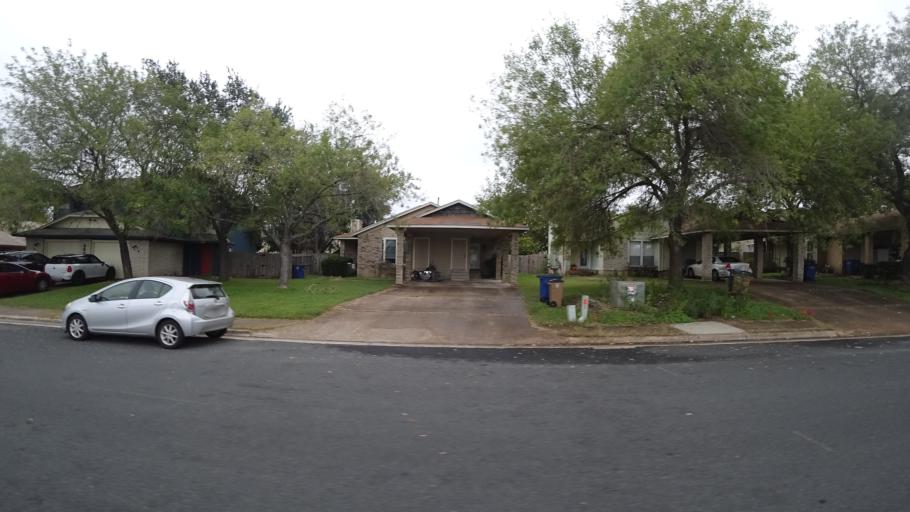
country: US
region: Texas
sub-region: Travis County
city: Shady Hollow
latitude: 30.2027
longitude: -97.8392
